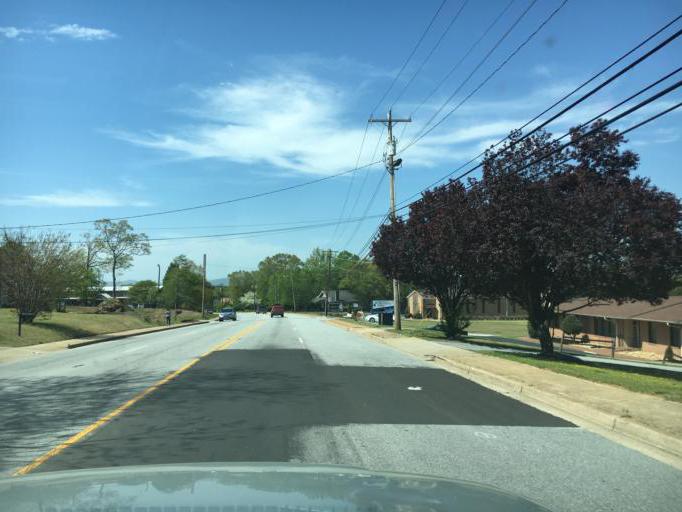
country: US
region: South Carolina
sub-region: Greenville County
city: Greer
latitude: 34.9514
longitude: -82.2258
